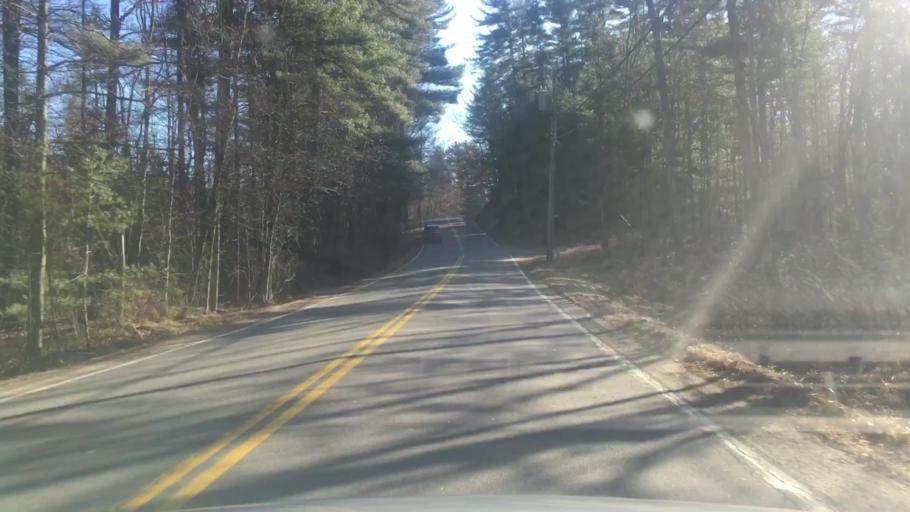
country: US
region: New Hampshire
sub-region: Rockingham County
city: Londonderry
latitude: 42.8905
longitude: -71.4098
